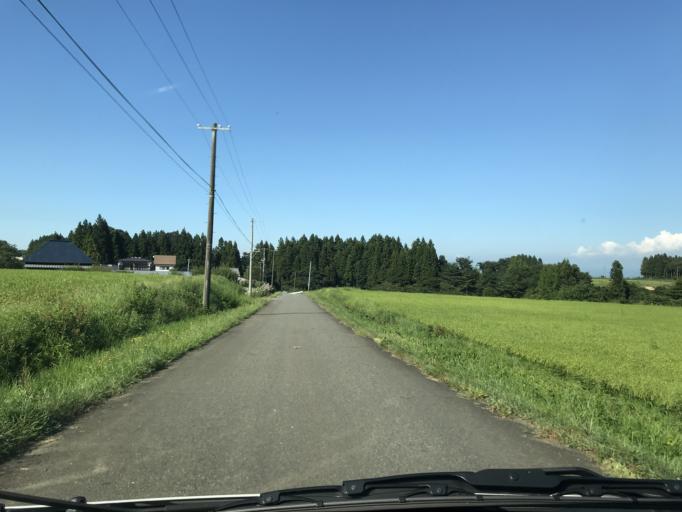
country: JP
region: Iwate
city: Mizusawa
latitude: 39.0695
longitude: 141.0455
